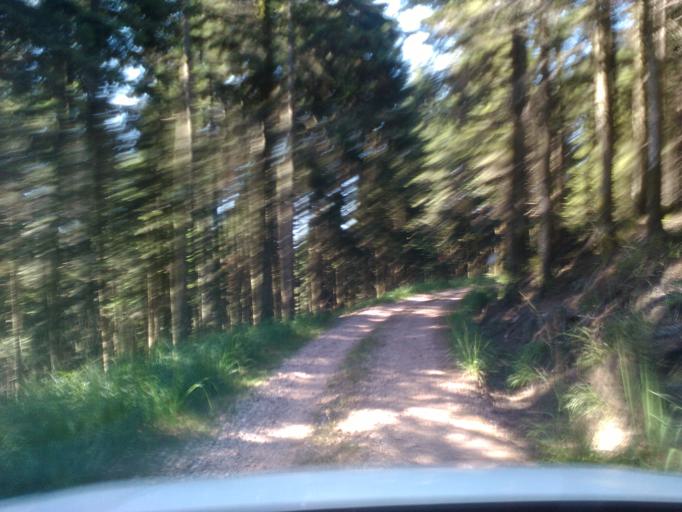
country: FR
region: Lorraine
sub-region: Departement des Vosges
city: Senones
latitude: 48.4357
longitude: 6.9821
